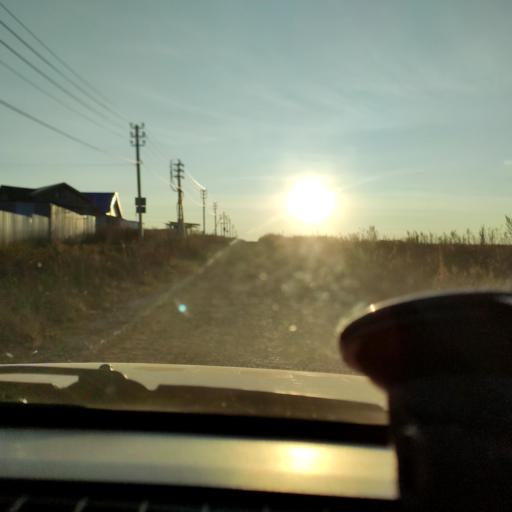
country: RU
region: Perm
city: Ferma
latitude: 57.9481
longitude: 56.3460
